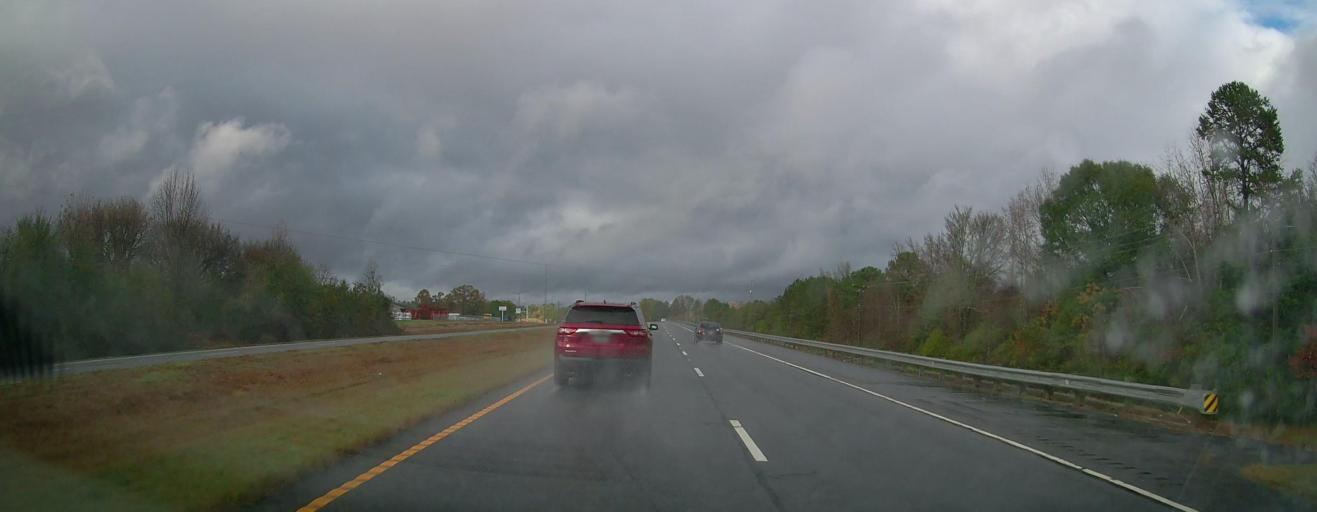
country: US
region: Georgia
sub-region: Clarke County
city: Country Club Estates
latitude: 34.0338
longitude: -83.4019
